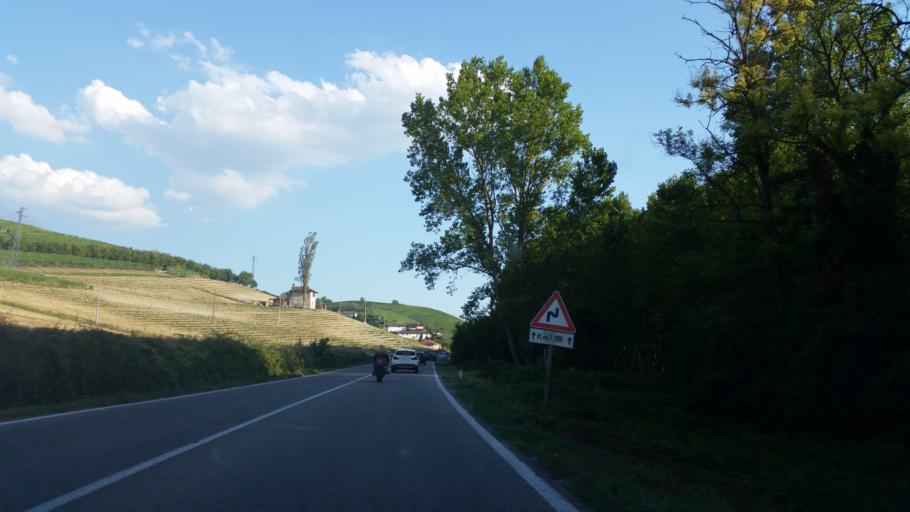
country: IT
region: Piedmont
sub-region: Provincia di Cuneo
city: Barbaresco
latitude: 44.7383
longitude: 8.0935
